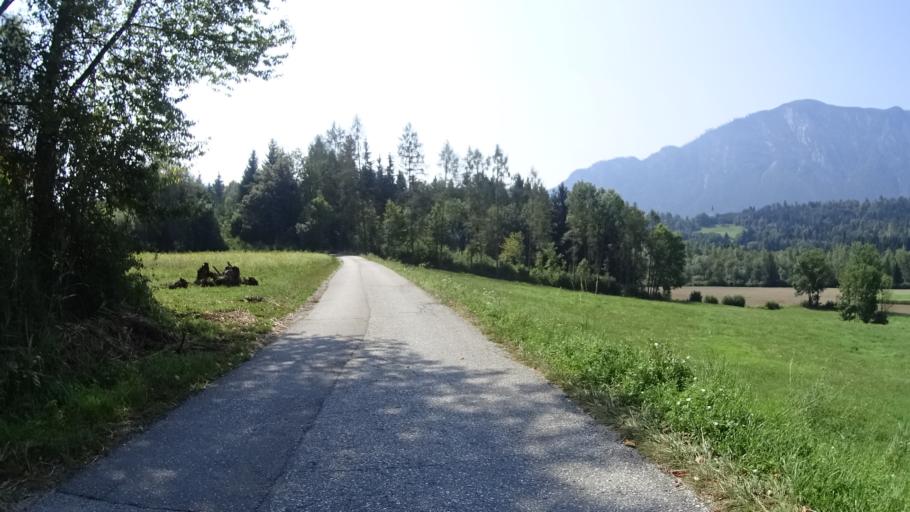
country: AT
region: Carinthia
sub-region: Politischer Bezirk Volkermarkt
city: Gallizien
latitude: 46.5629
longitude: 14.5458
